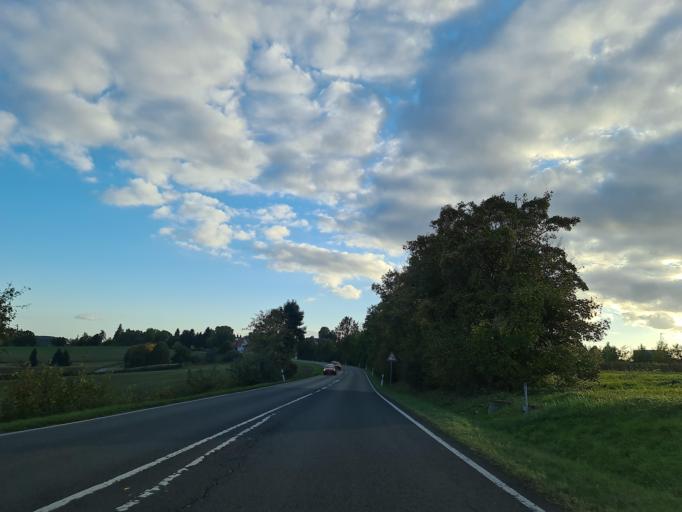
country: DE
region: Thuringia
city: Teichwitz
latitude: 50.7437
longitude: 12.0869
